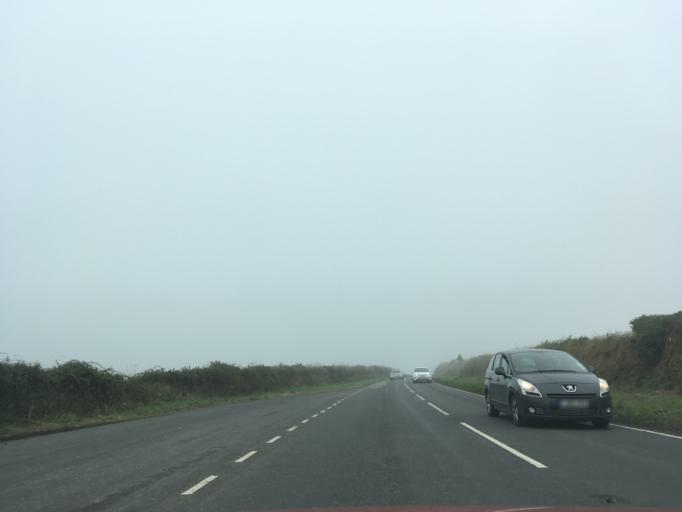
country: GB
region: Wales
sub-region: Pembrokeshire
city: Llanrhian
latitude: 51.8709
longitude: -5.1501
